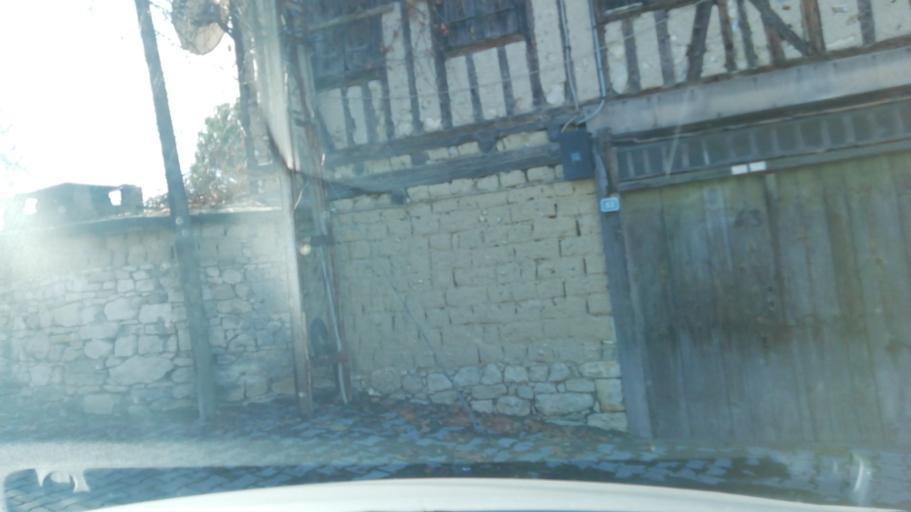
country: TR
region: Karabuk
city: Safranbolu
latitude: 41.2326
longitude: 32.7786
